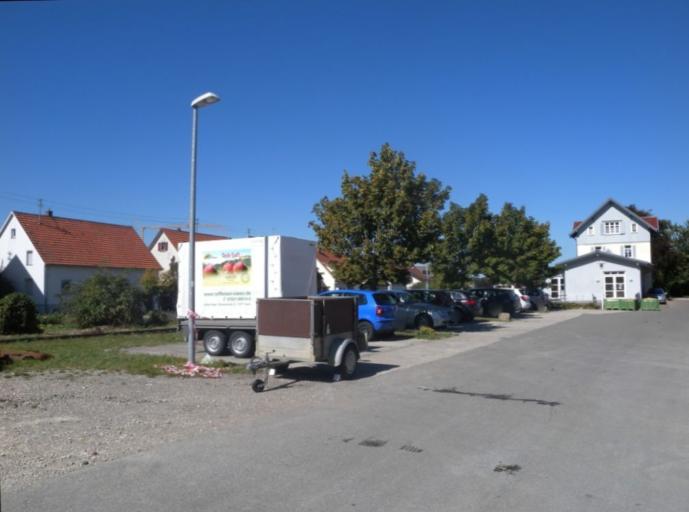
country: DE
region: Baden-Wuerttemberg
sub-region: Regierungsbezirk Stuttgart
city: Owen
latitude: 48.5863
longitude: 9.4480
